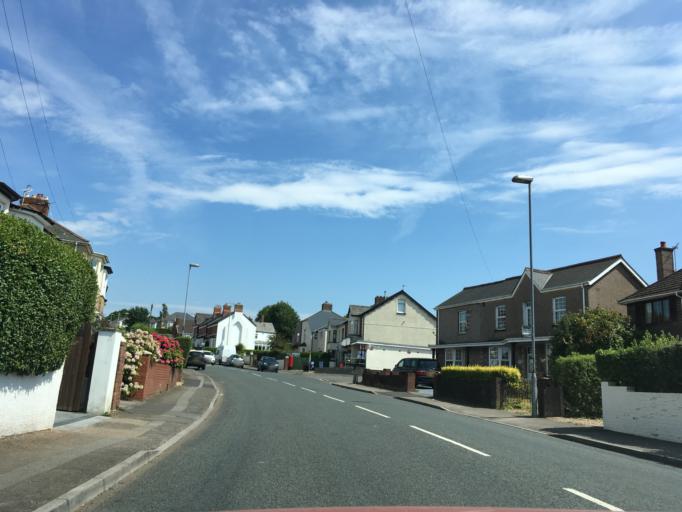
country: GB
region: Wales
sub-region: Newport
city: Caerleon
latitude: 51.5931
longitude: -2.9595
